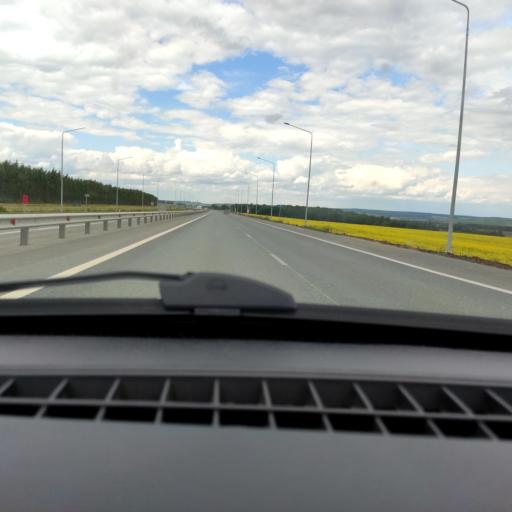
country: RU
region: Bashkortostan
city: Tolbazy
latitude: 53.9802
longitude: 55.9205
